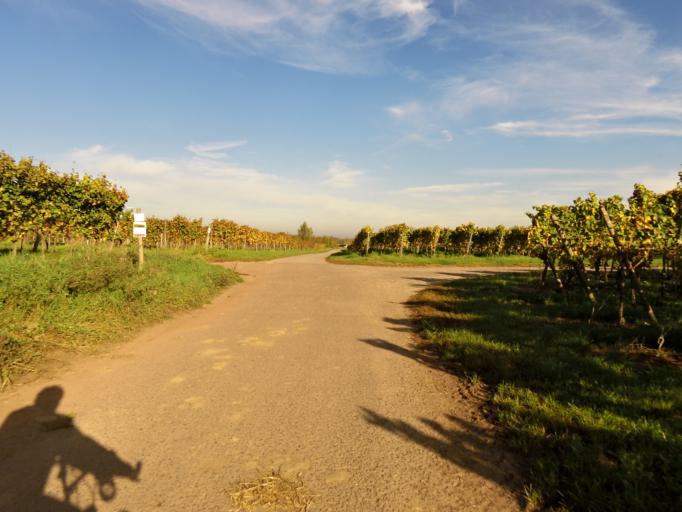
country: DE
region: Rheinland-Pfalz
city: Niederkirchen bei Deidesheim
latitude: 49.4175
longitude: 8.2084
